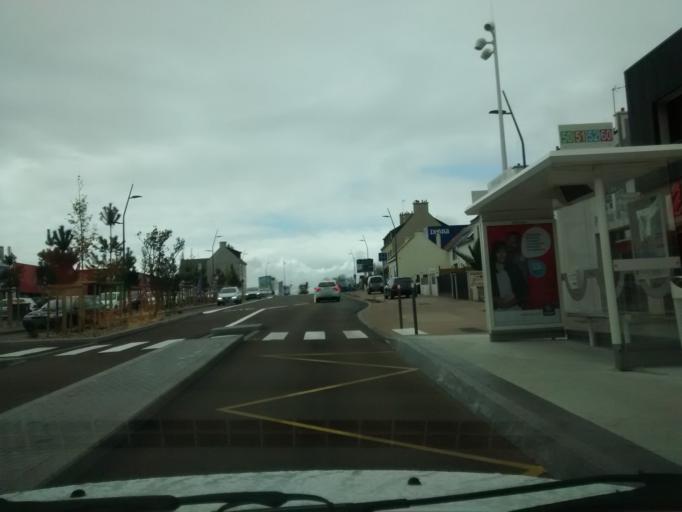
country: FR
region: Brittany
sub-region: Departement du Morbihan
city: Queven
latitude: 47.7663
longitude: -3.4011
